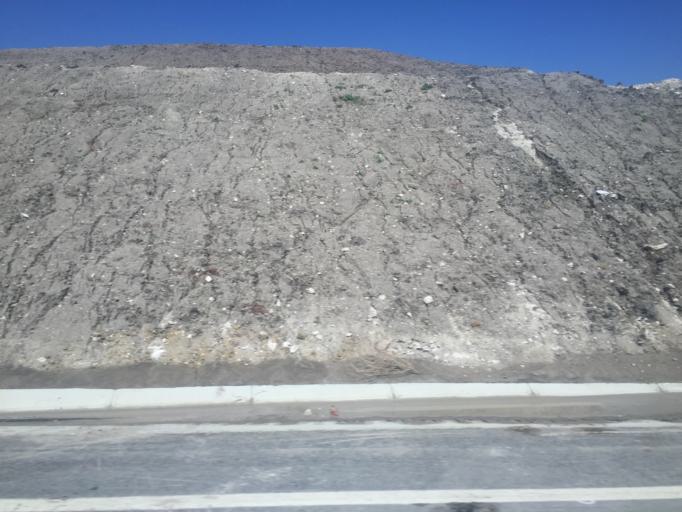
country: TR
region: Balikesir
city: Gobel
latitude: 39.9690
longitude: 28.1612
